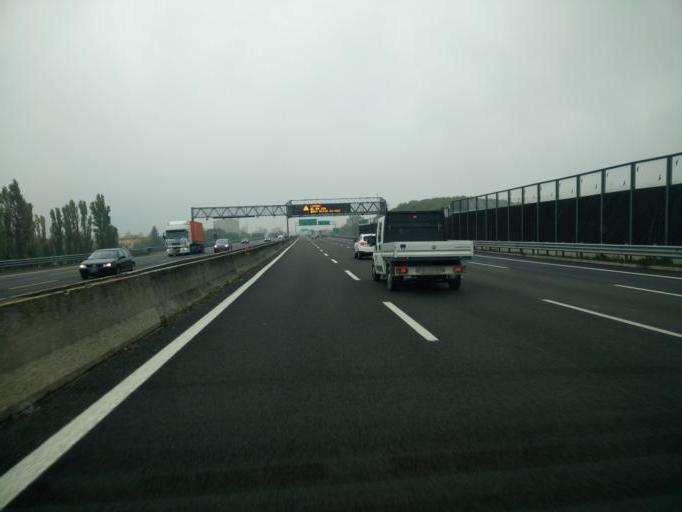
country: IT
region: Emilia-Romagna
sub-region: Provincia di Modena
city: Baggiovara
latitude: 44.6448
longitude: 10.8685
